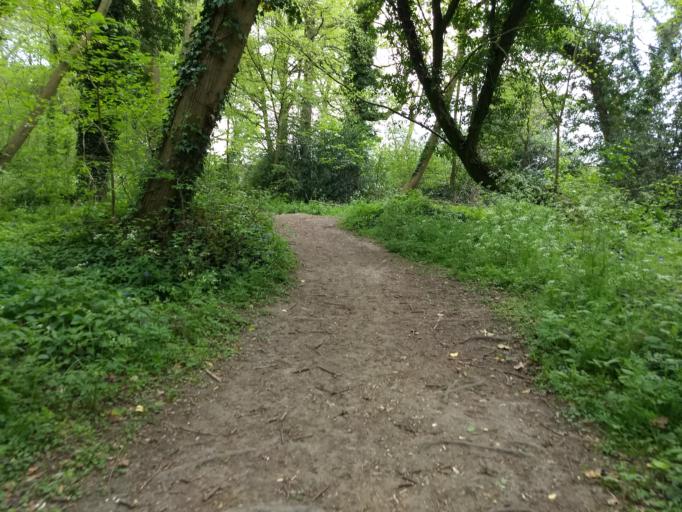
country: GB
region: England
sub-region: Hertfordshire
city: Hemel Hempstead
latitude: 51.7613
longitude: -0.4442
